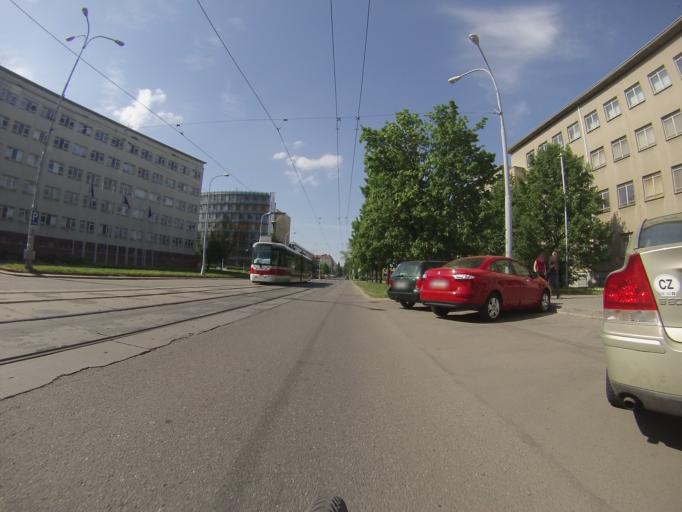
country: CZ
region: South Moravian
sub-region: Mesto Brno
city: Brno
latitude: 49.2079
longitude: 16.5954
